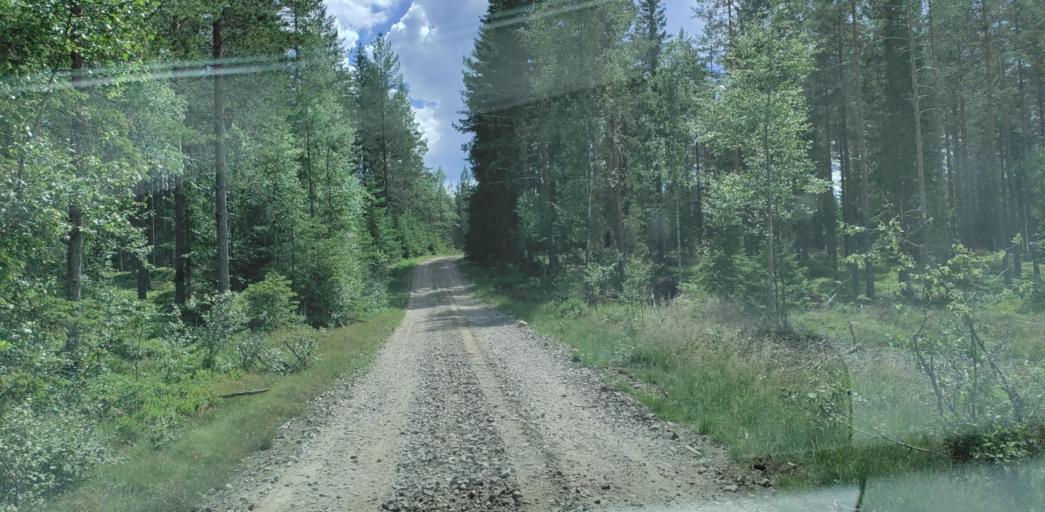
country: SE
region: Vaermland
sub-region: Hagfors Kommun
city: Ekshaerad
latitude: 60.0731
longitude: 13.3457
